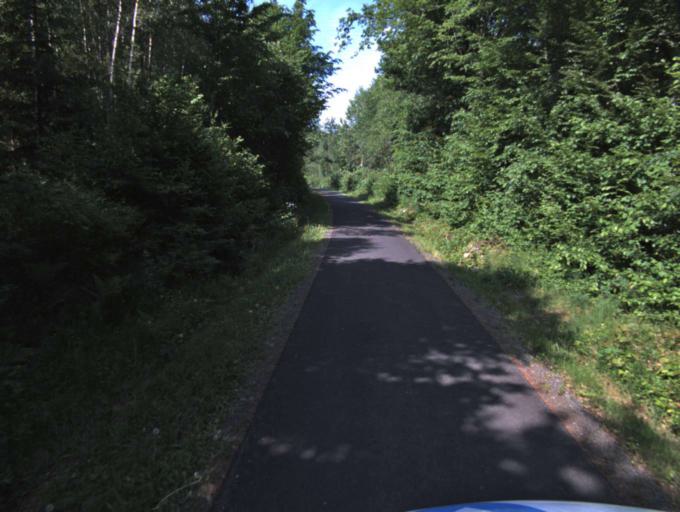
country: SE
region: Skane
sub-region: Kristianstads Kommun
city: Tollarp
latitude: 56.1882
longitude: 14.2877
